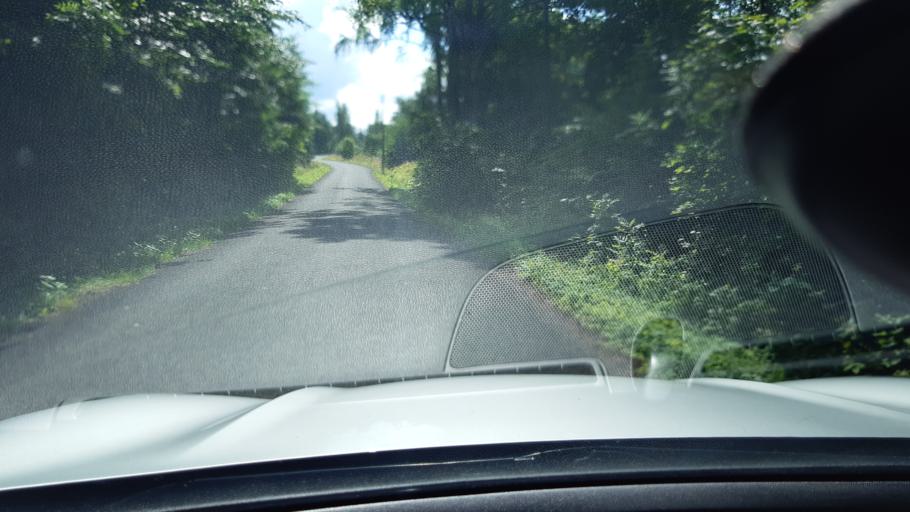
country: EE
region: Raplamaa
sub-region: Kehtna vald
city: Kehtna
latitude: 58.9384
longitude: 24.8966
